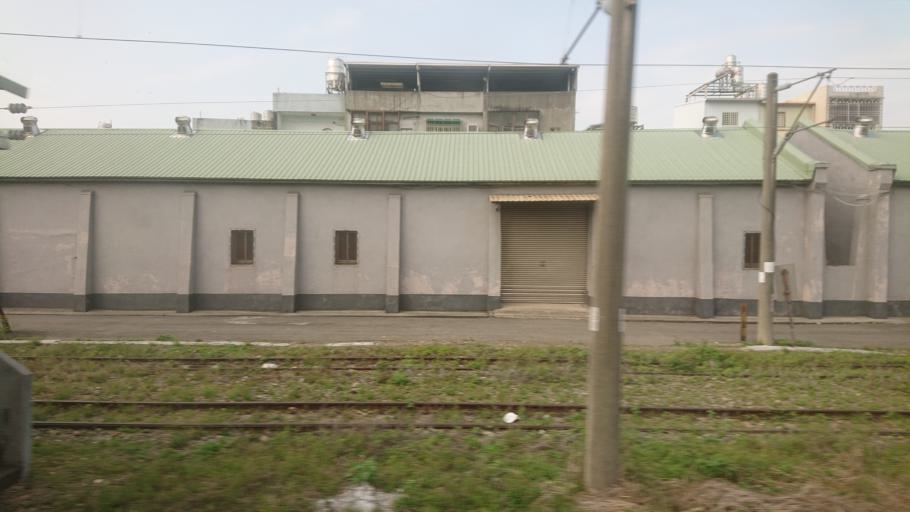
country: TW
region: Taiwan
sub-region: Nantou
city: Nantou
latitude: 23.8541
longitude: 120.5931
